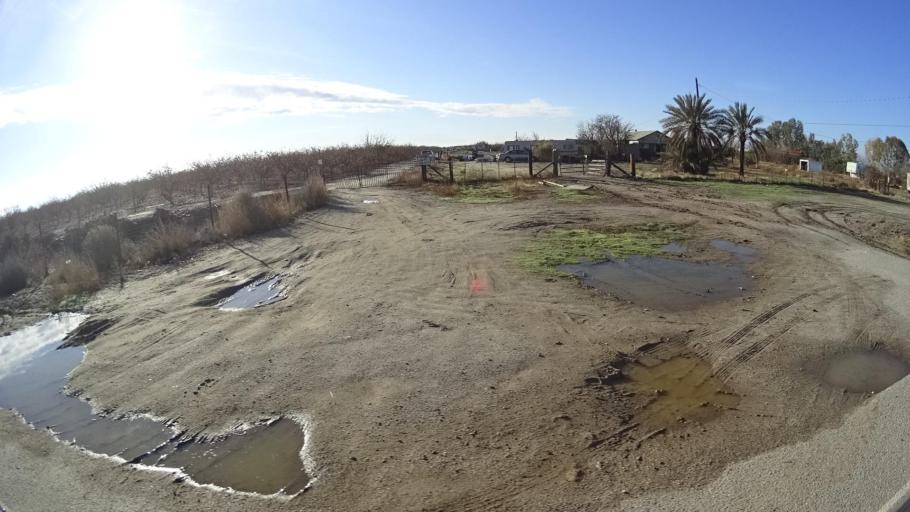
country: US
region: California
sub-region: Kern County
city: Delano
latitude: 35.7757
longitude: -119.3380
